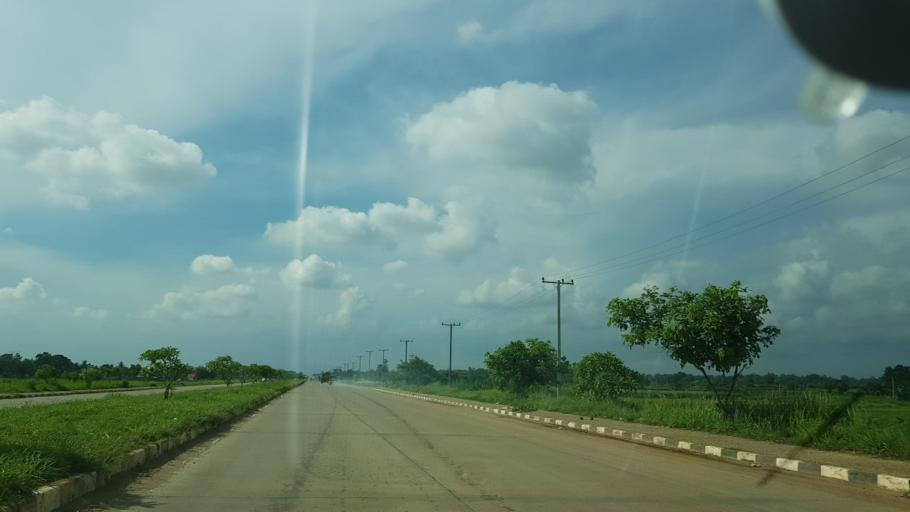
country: TH
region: Nong Khai
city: Nong Khai
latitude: 17.8901
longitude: 102.7208
